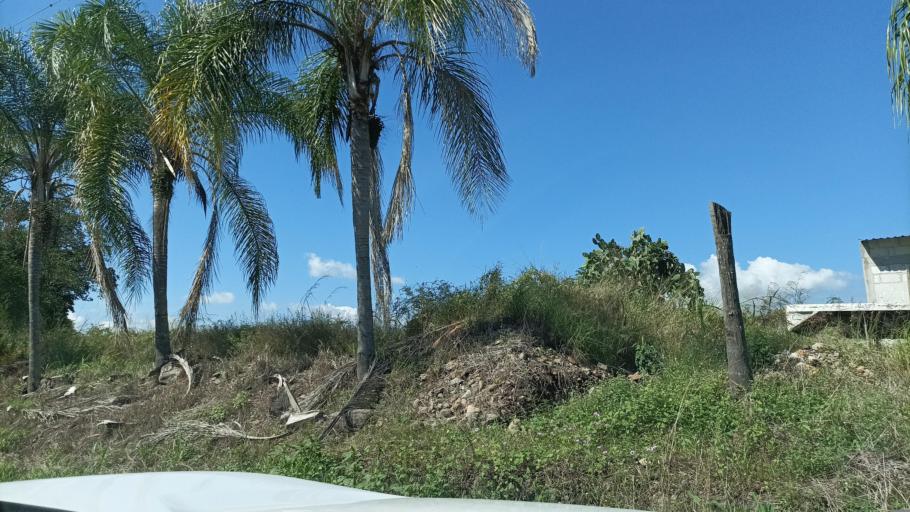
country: MX
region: Veracruz
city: Paso del Macho
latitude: 18.9694
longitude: -96.7325
